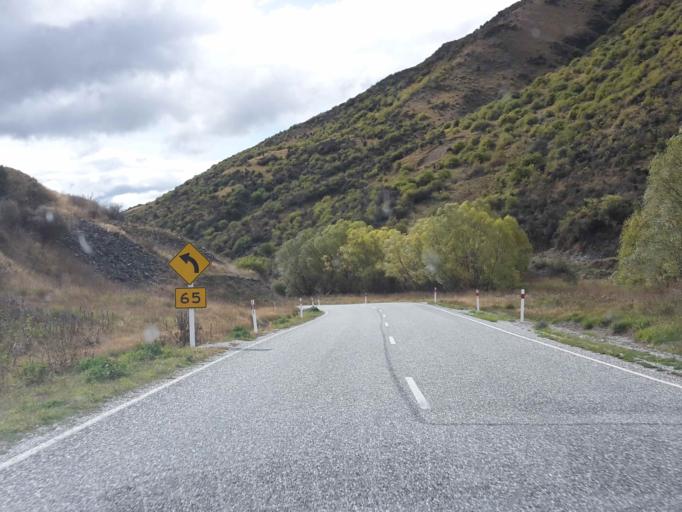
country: NZ
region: Otago
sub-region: Queenstown-Lakes District
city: Arrowtown
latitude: -44.9285
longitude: 168.9709
